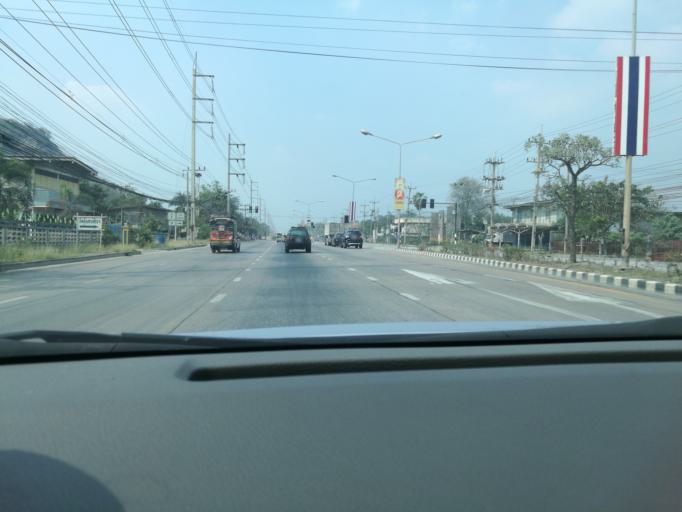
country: TH
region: Sara Buri
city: Phra Phutthabat
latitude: 14.6987
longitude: 100.8626
